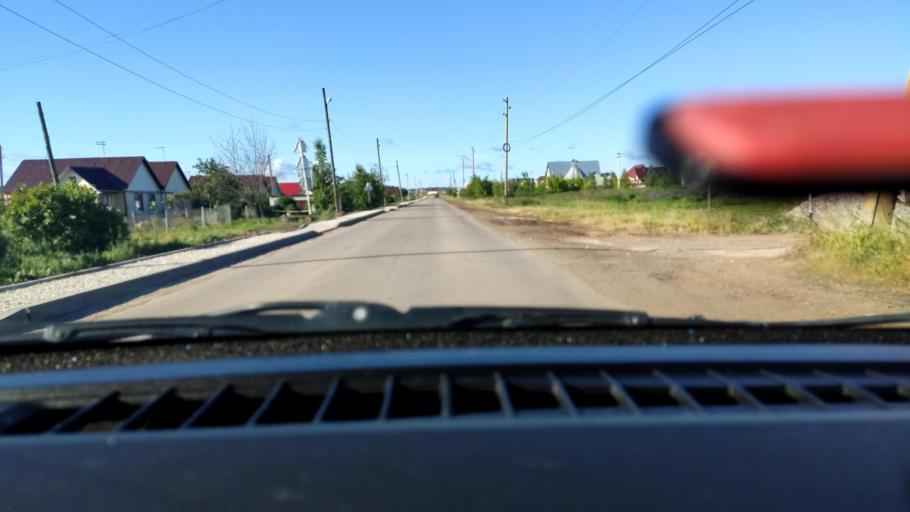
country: RU
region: Perm
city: Kultayevo
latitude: 57.8704
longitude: 55.9176
